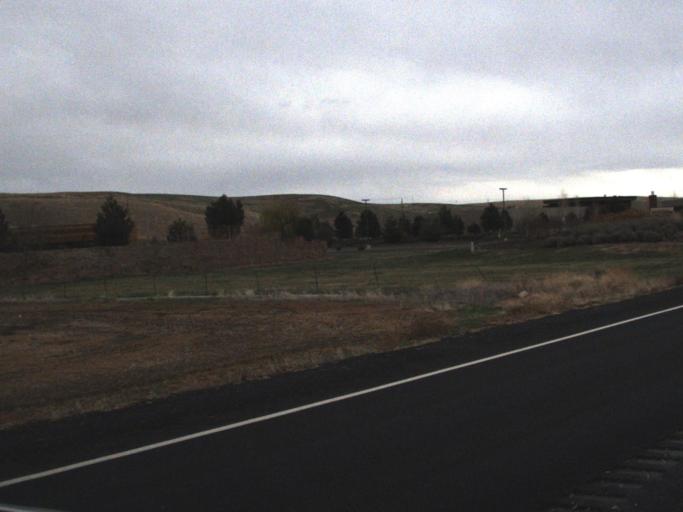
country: US
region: Washington
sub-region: Walla Walla County
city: Garrett
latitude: 46.0535
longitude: -118.5598
